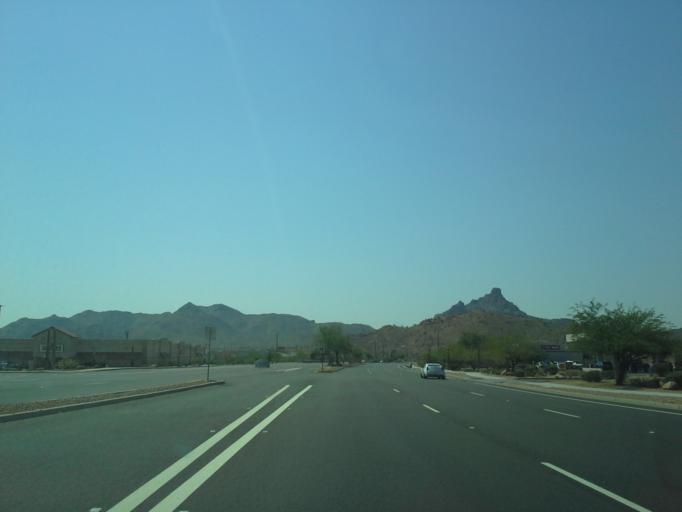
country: US
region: Arizona
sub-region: Maricopa County
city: Fountain Hills
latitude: 33.5717
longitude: -111.7126
